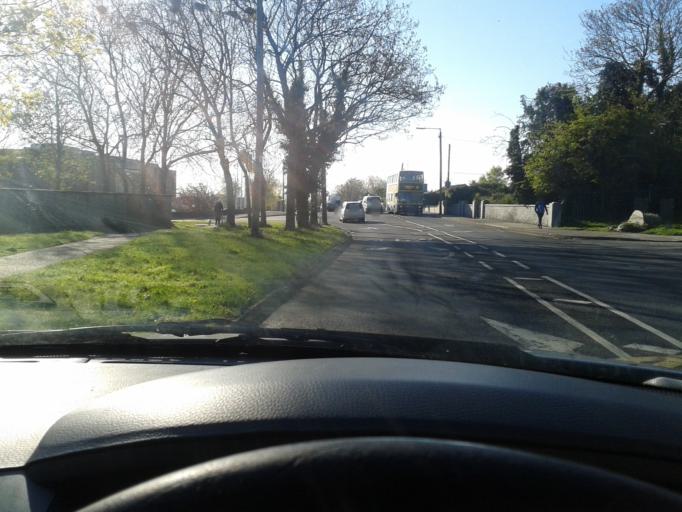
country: IE
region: Leinster
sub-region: Fingal County
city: Swords
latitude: 53.4629
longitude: -6.2331
